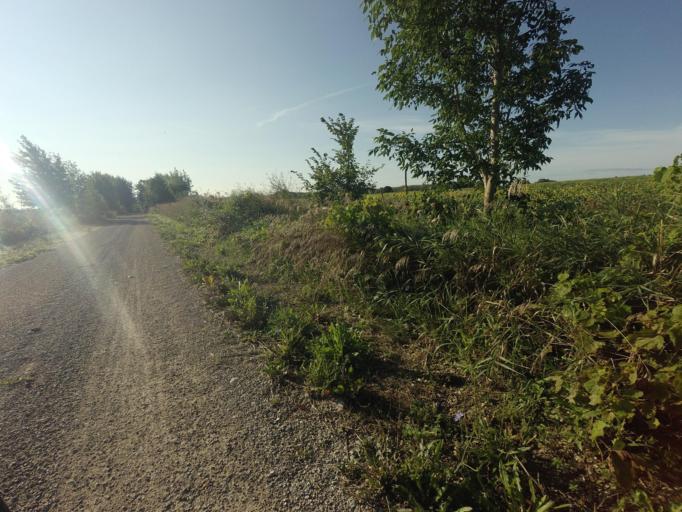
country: CA
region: Ontario
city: Goderich
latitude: 43.7599
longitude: -81.5210
